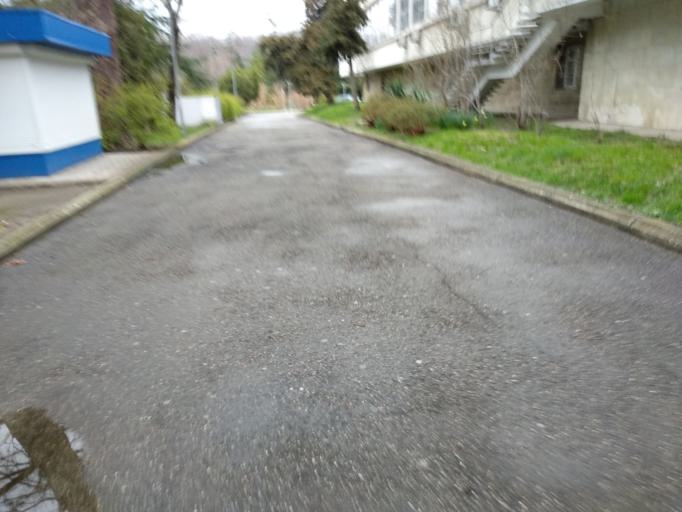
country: RU
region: Krasnodarskiy
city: Novomikhaylovskiy
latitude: 44.2579
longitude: 38.8227
